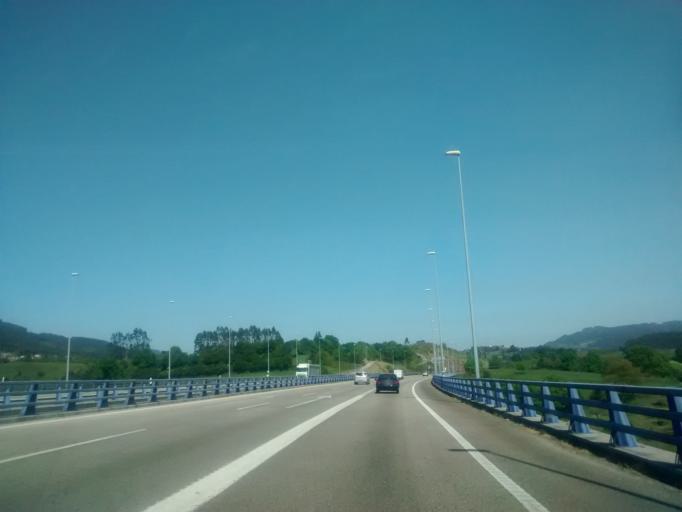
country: ES
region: Asturias
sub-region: Province of Asturias
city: Villaviciosa
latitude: 43.4671
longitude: -5.4830
